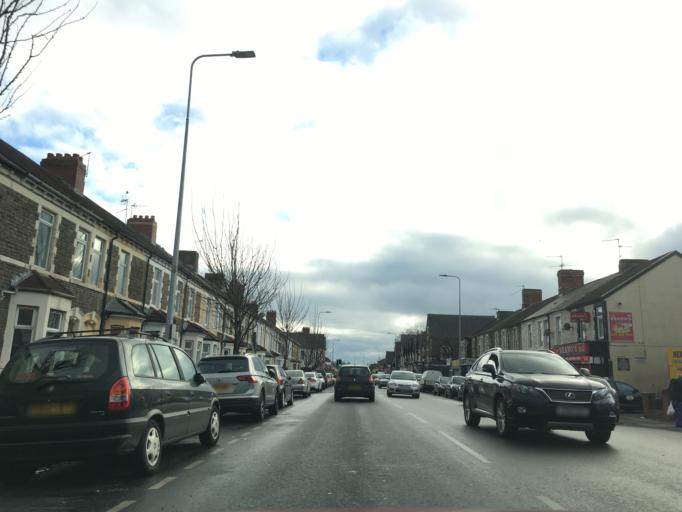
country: GB
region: Wales
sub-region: Cardiff
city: Cardiff
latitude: 51.4721
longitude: -3.1866
